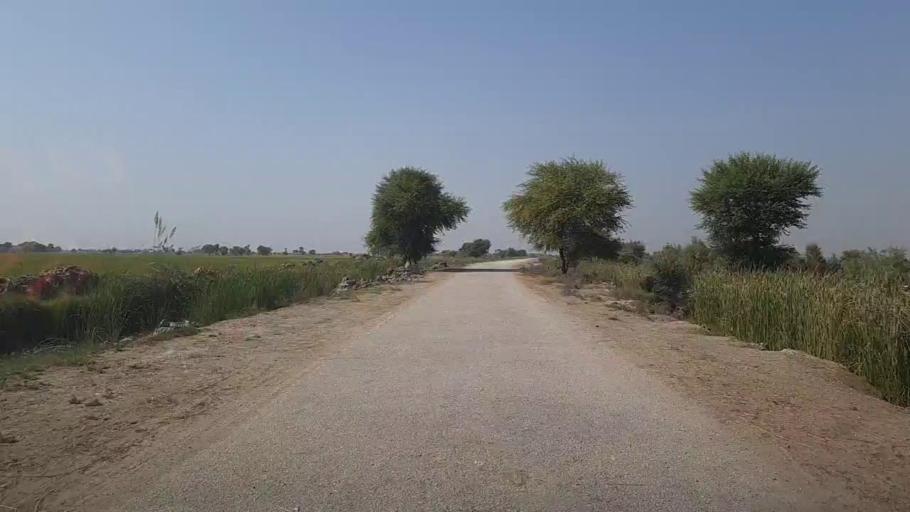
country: PK
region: Sindh
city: Kandhkot
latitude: 28.3949
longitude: 69.2746
